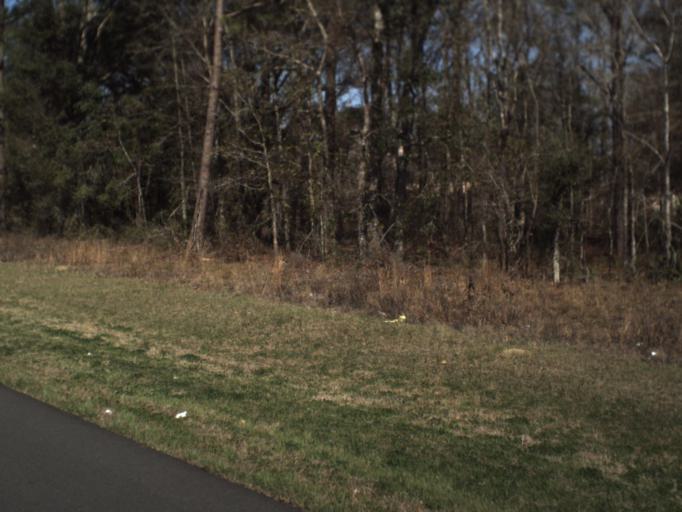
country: US
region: Florida
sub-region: Jackson County
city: Malone
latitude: 30.8391
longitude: -85.0624
